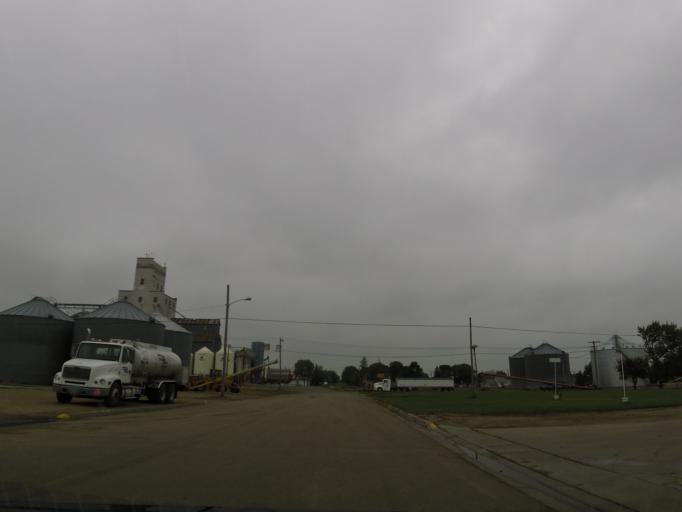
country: US
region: Minnesota
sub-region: Marshall County
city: Warren
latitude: 48.3350
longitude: -96.8167
